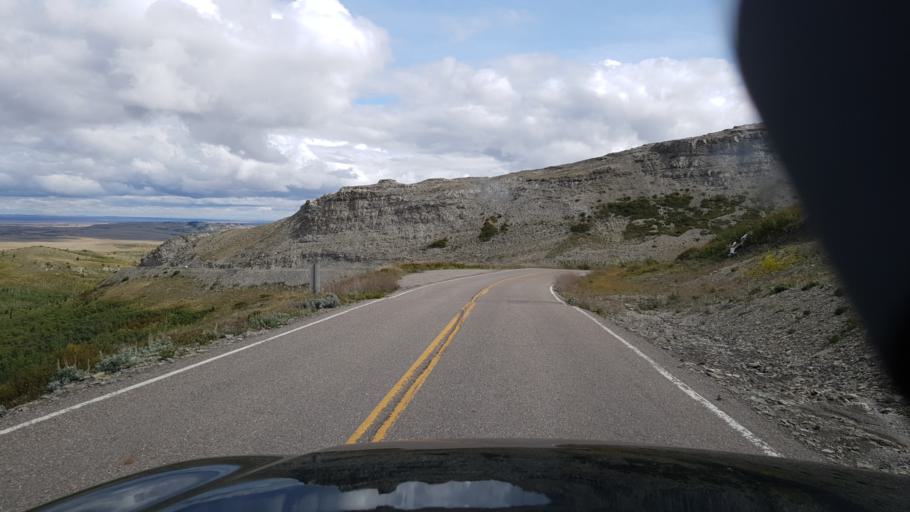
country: US
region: Montana
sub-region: Glacier County
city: South Browning
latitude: 48.5430
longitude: -113.3013
